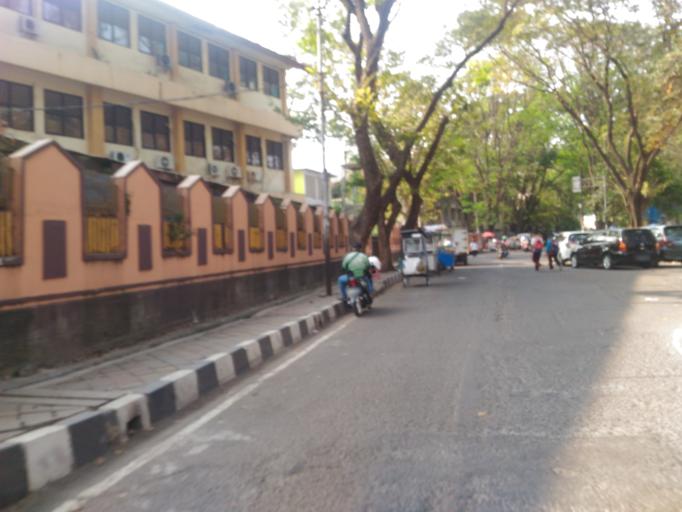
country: ID
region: Banten
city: Tangerang
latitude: -6.1717
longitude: 106.6331
